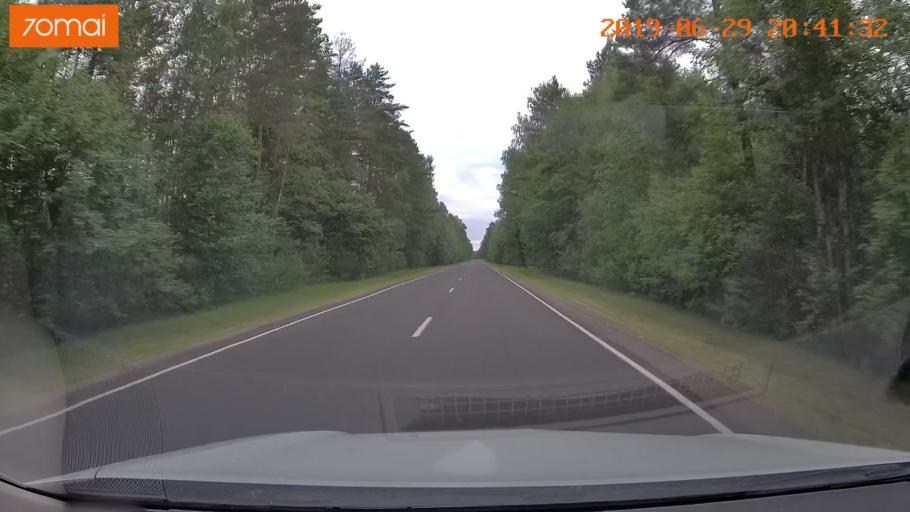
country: BY
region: Brest
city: Hantsavichy
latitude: 52.5869
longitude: 26.3382
